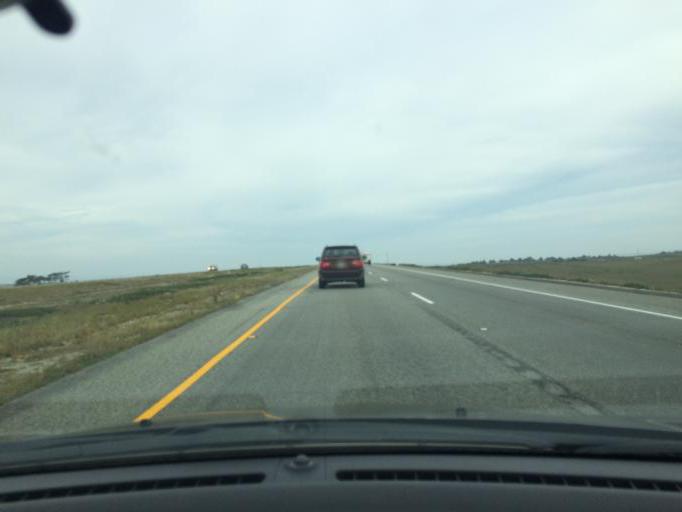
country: US
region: California
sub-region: Monterey County
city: Marina
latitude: 36.7066
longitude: -121.7990
